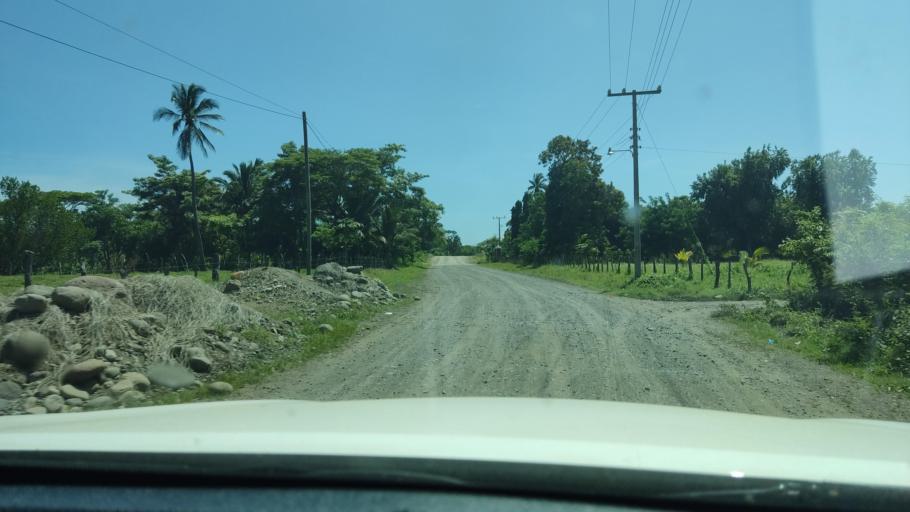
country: SV
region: Ahuachapan
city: San Francisco Menendez
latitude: 13.7655
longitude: -90.1615
